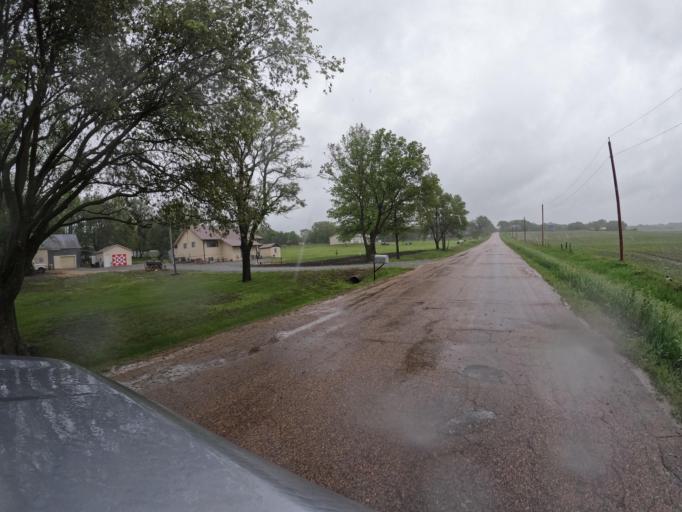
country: US
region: Nebraska
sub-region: Gage County
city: Wymore
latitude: 40.1177
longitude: -96.6809
